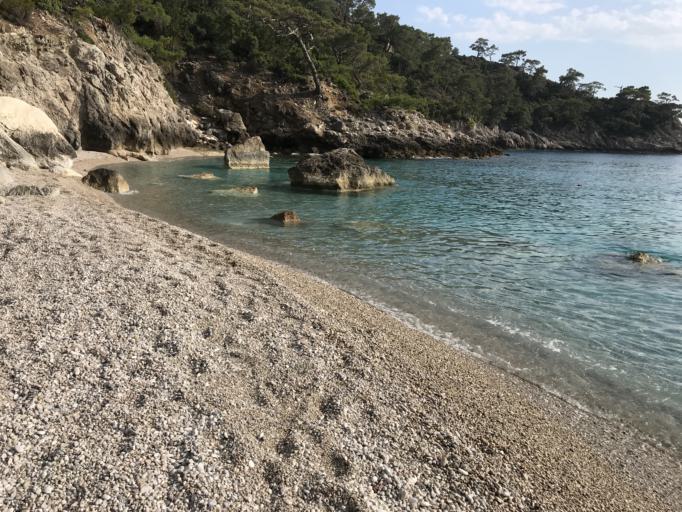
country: TR
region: Mugla
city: OEluedeniz
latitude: 36.4399
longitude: 29.1315
